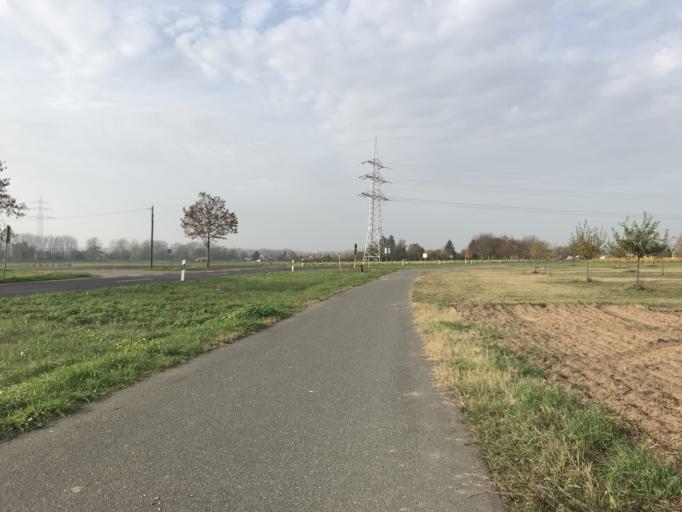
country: DE
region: Hesse
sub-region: Regierungsbezirk Darmstadt
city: Ginsheim-Gustavsburg
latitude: 49.9598
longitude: 8.3643
